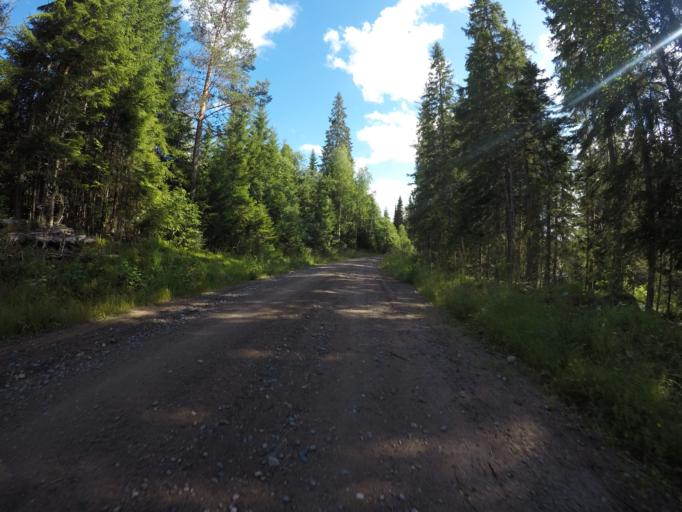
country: SE
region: Dalarna
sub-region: Ludvika Kommun
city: Abborrberget
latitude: 60.0090
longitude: 14.6098
